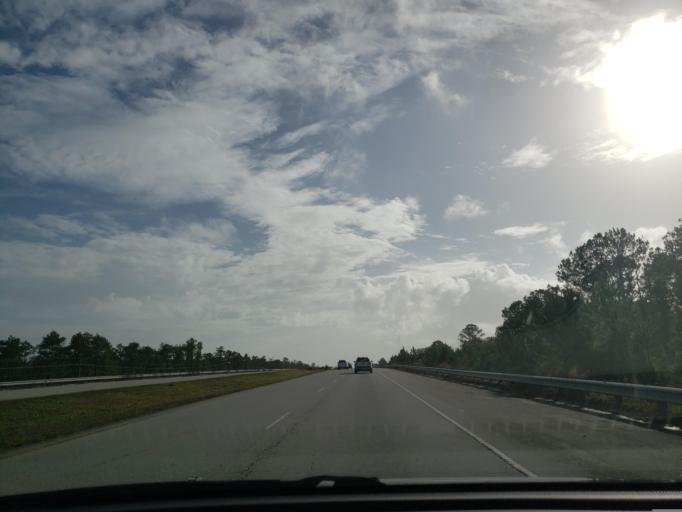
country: US
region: North Carolina
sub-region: Onslow County
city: Sneads Ferry
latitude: 34.6384
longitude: -77.4795
